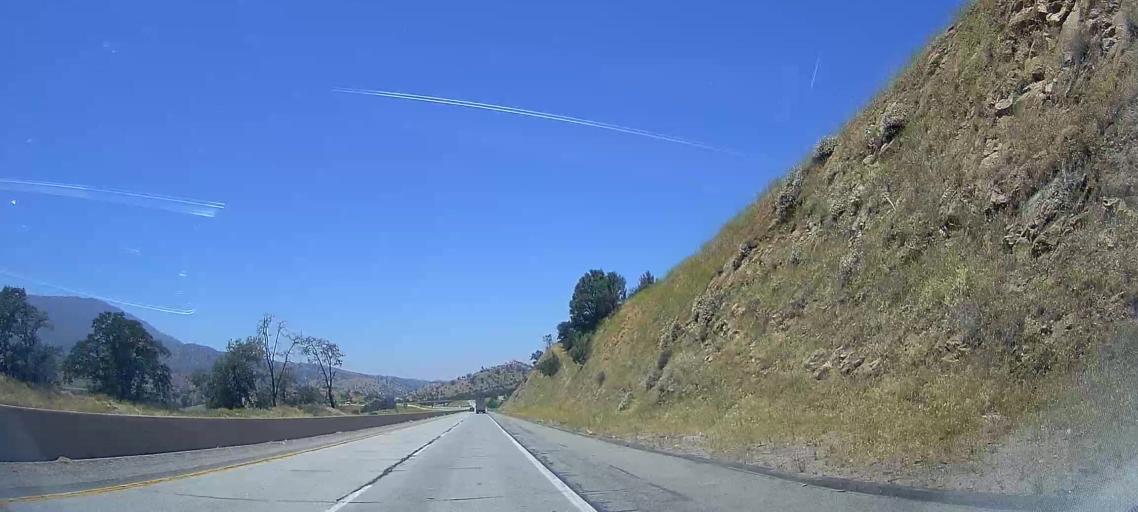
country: US
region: California
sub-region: Kern County
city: Golden Hills
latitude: 35.1957
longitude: -118.5147
